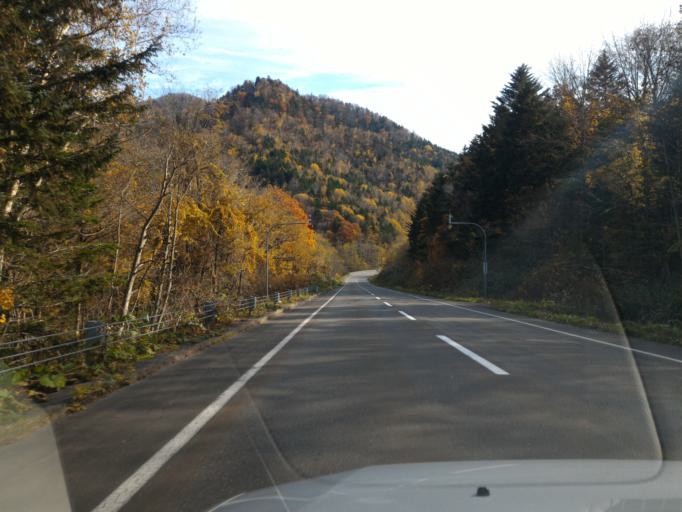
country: JP
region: Hokkaido
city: Shimo-furano
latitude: 43.3635
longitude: 142.2385
